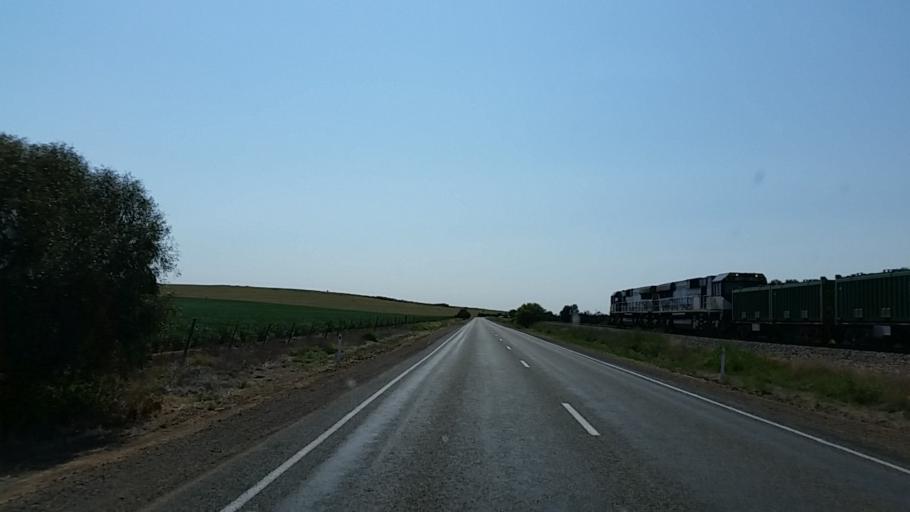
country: AU
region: South Australia
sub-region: Port Pirie City and Dists
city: Crystal Brook
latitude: -33.2467
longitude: 138.3699
